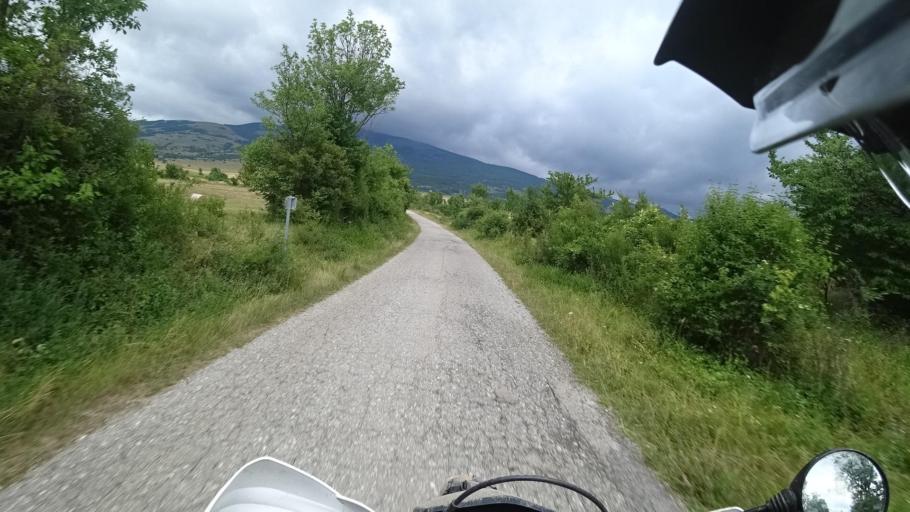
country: HR
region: Zadarska
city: Gracac
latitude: 44.5292
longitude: 15.8242
